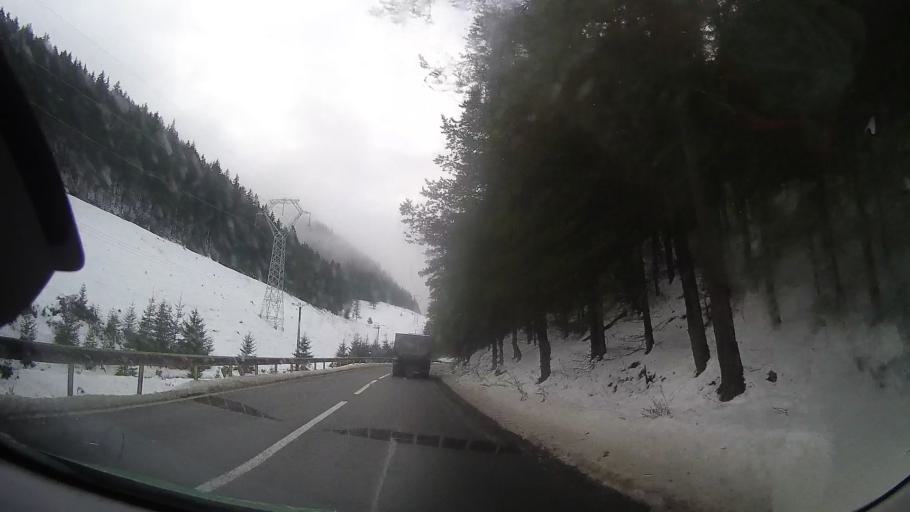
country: RO
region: Neamt
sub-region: Comuna Bicaz Chei
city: Bicaz Chei
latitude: 46.7781
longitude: 25.7642
